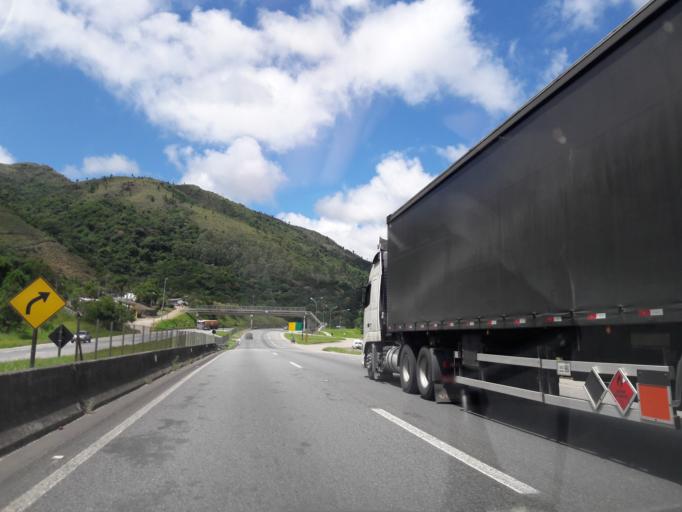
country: BR
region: Parana
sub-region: Campina Grande Do Sul
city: Campina Grande do Sul
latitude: -25.1378
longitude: -48.8567
